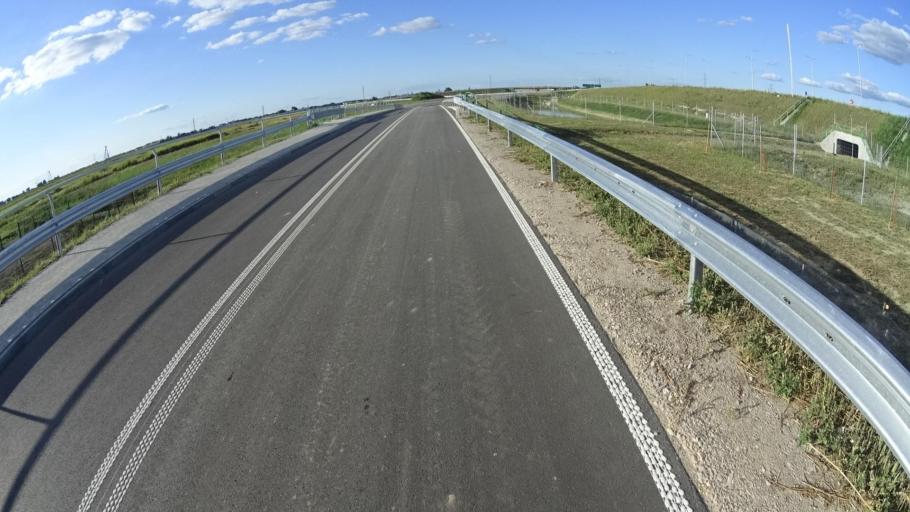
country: PL
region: Masovian Voivodeship
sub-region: Powiat piaseczynski
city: Lesznowola
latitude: 52.0835
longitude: 20.9657
